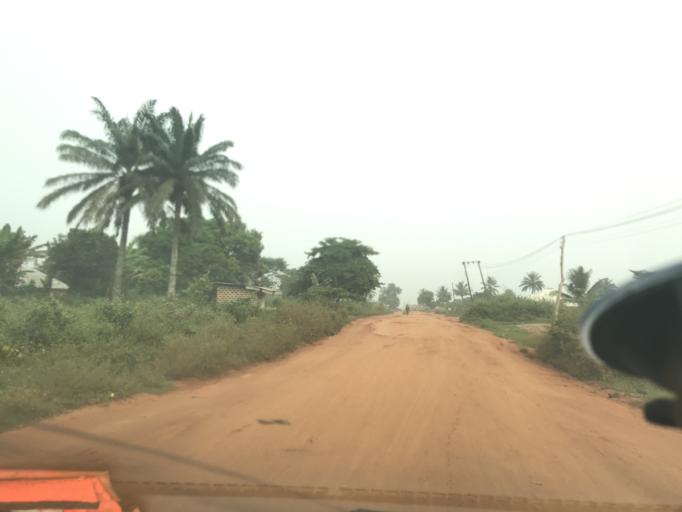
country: NG
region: Ogun
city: Ado Odo
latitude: 6.5577
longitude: 2.9441
